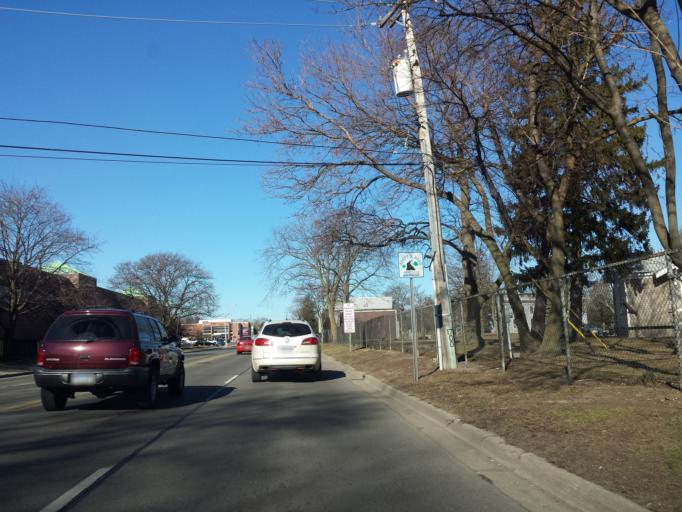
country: US
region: Michigan
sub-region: Oakland County
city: Berkley
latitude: 42.5035
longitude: -83.1735
